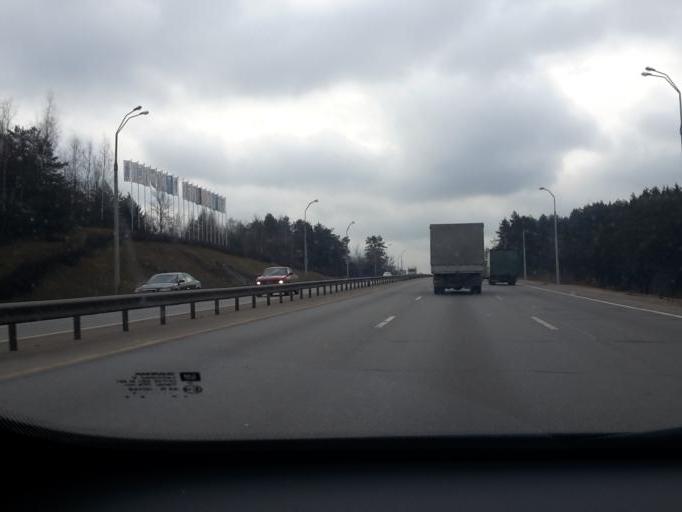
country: BY
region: Minsk
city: Borovlyany
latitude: 53.9286
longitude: 27.6780
